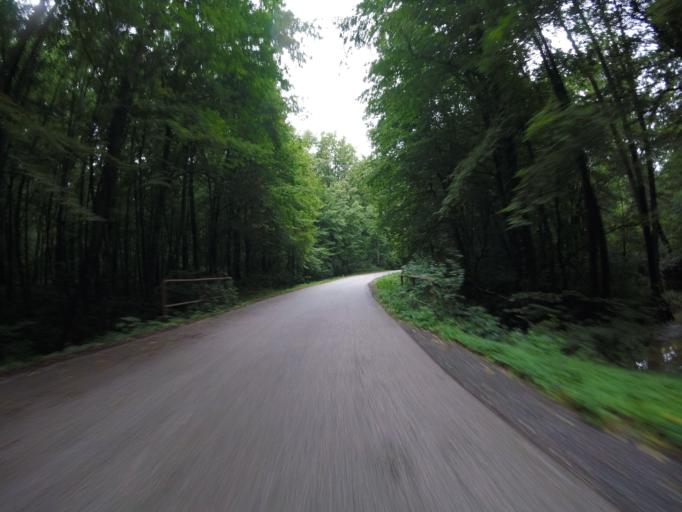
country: HR
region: Zagrebacka
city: Mraclin
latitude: 45.6137
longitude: 16.0934
